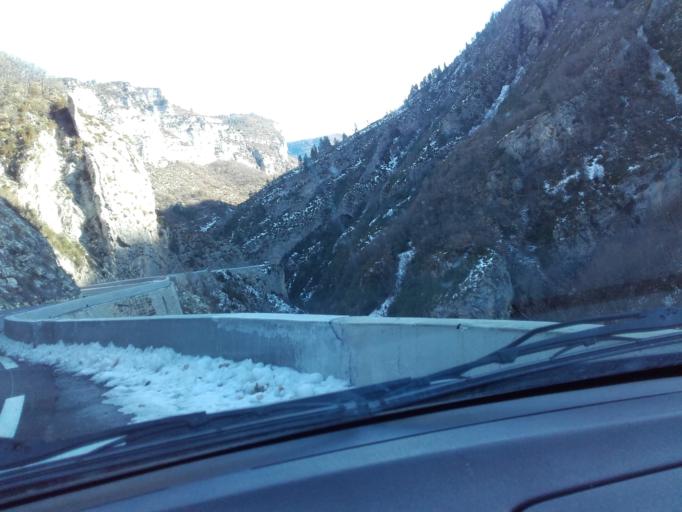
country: FR
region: Provence-Alpes-Cote d'Azur
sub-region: Departement des Alpes-de-Haute-Provence
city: Annot
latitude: 43.9369
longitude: 6.6810
